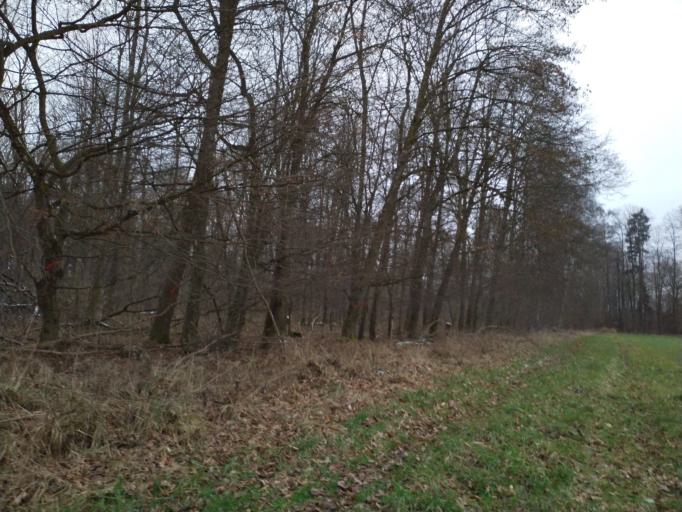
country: DE
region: Bavaria
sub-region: Swabia
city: Offingen
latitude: 48.4919
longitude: 10.3418
